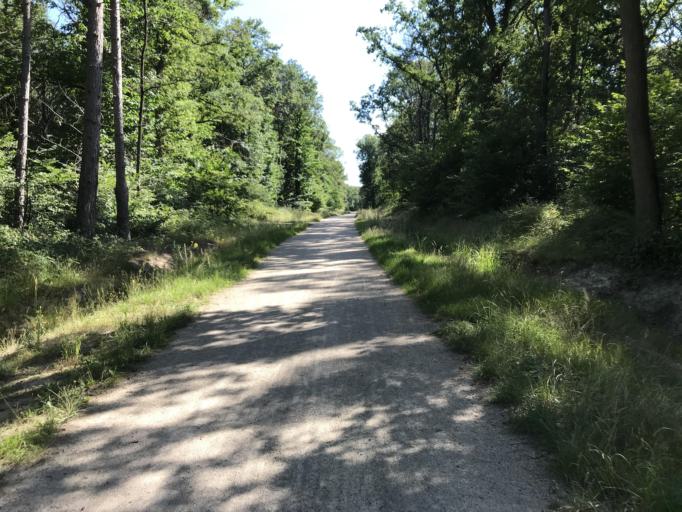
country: FR
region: Ile-de-France
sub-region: Departement de l'Essonne
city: Bondoufle
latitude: 48.6306
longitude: 2.3835
